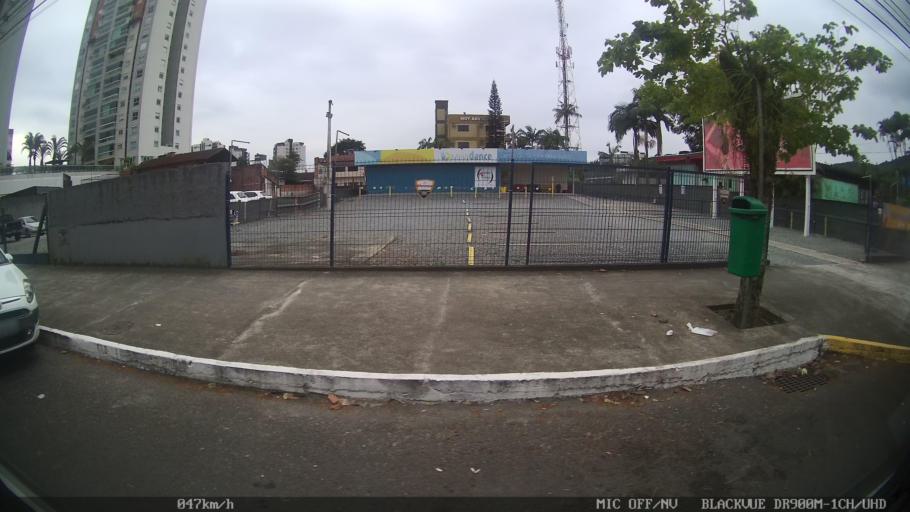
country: BR
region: Santa Catarina
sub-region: Joinville
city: Joinville
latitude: -26.2962
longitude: -48.8433
